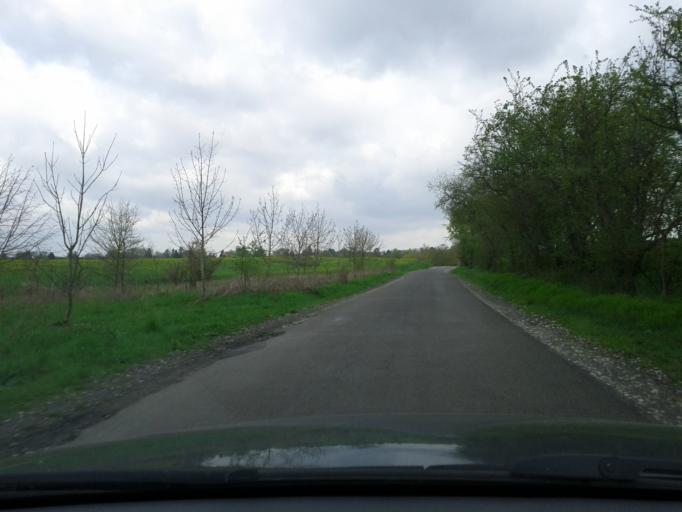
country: DE
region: Brandenburg
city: Schoneiche
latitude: 52.4837
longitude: 13.6811
